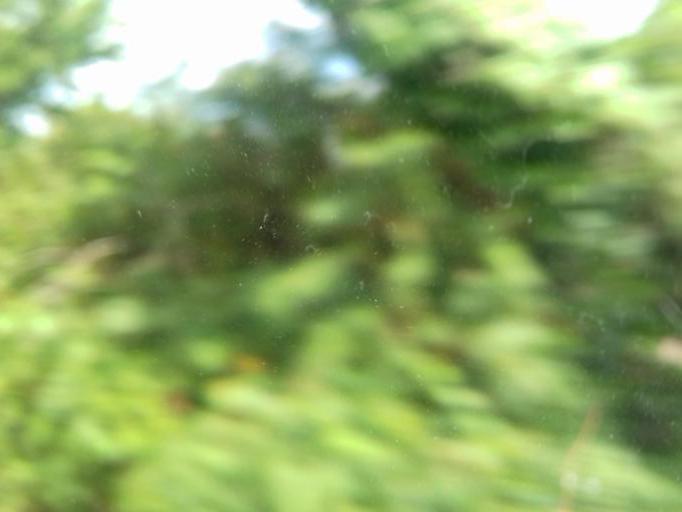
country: IE
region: Leinster
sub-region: Loch Garman
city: Loch Garman
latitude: 52.3304
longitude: -6.6245
